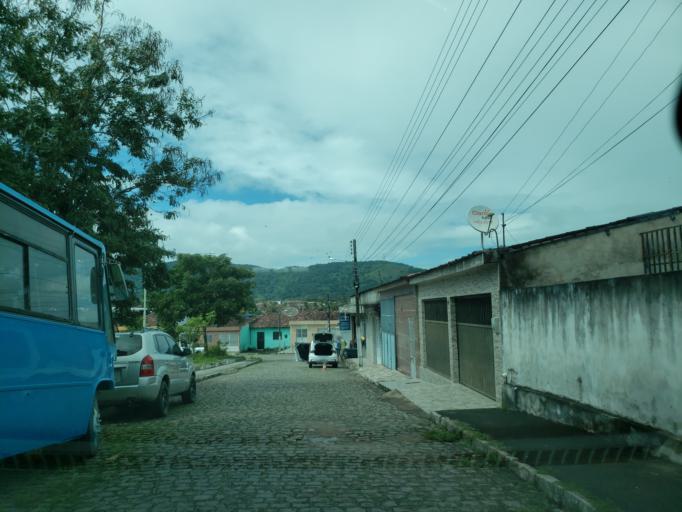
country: BR
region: Alagoas
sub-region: Uniao Dos Palmares
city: Uniao dos Palmares
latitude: -9.1596
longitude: -36.0238
